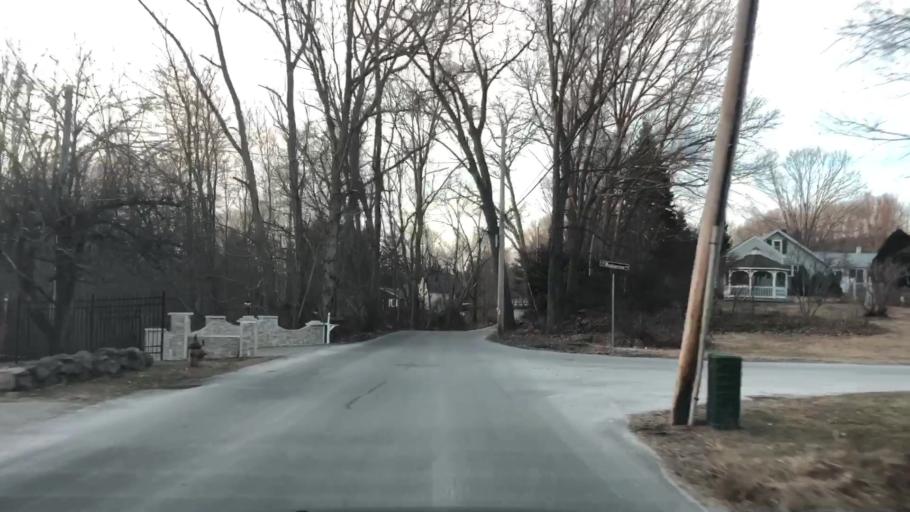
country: US
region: Massachusetts
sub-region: Essex County
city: North Andover
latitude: 42.6983
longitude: -71.0762
